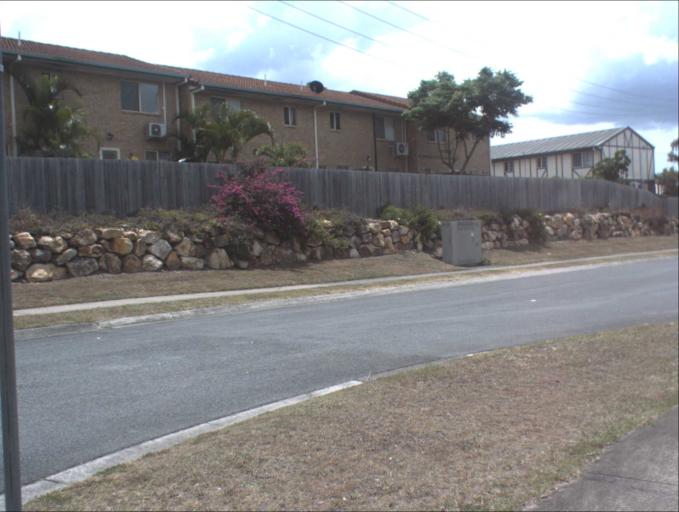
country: AU
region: Queensland
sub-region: Logan
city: Beenleigh
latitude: -27.7004
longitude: 153.1684
